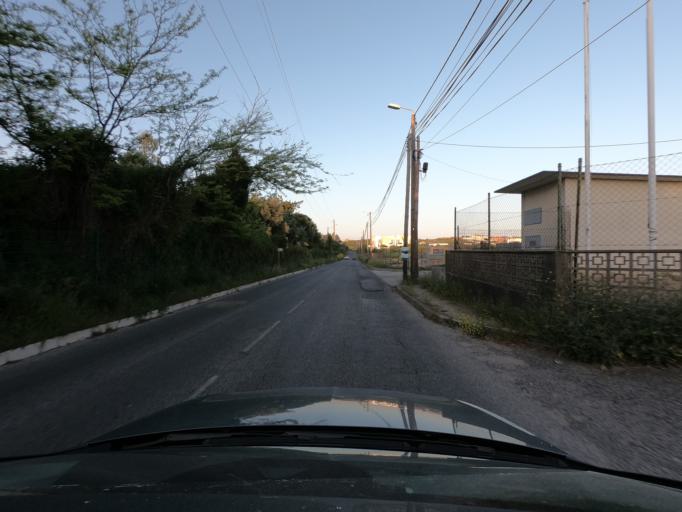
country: PT
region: Lisbon
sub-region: Sintra
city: Sintra
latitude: 38.7601
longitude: -9.3703
